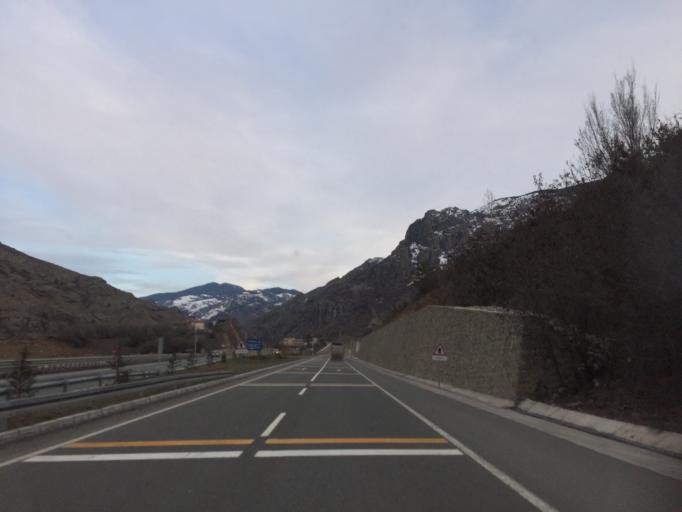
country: TR
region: Gumushane
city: Gumushkhane
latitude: 40.5043
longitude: 39.4252
